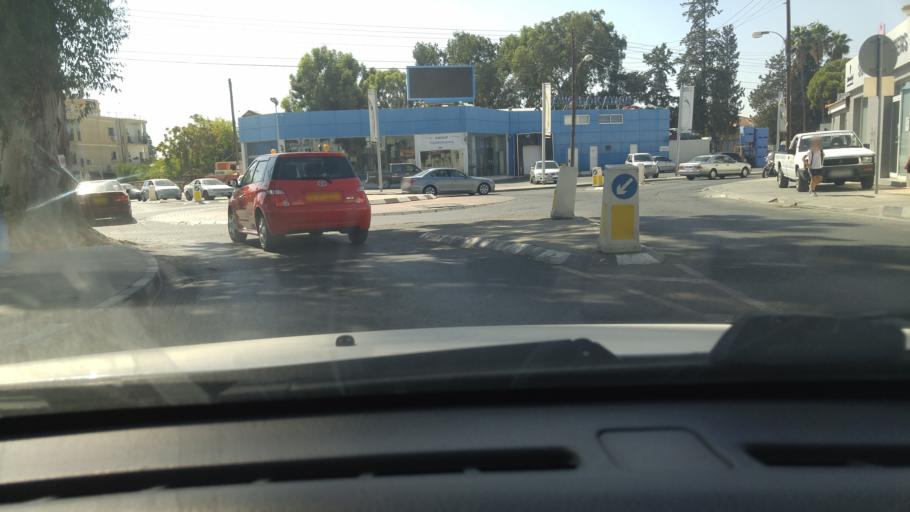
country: CY
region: Limassol
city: Limassol
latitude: 34.6736
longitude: 33.0338
